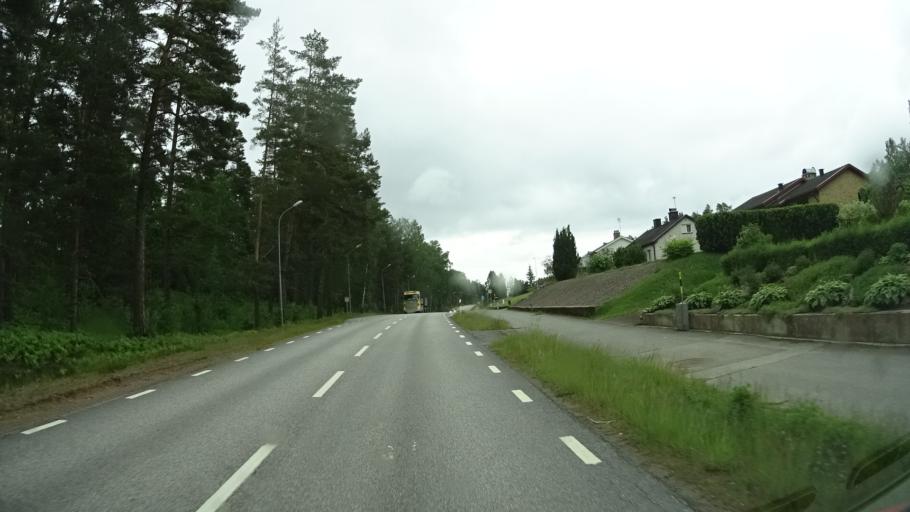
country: SE
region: Kalmar
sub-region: Hultsfreds Kommun
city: Hultsfred
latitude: 57.5456
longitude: 15.7375
